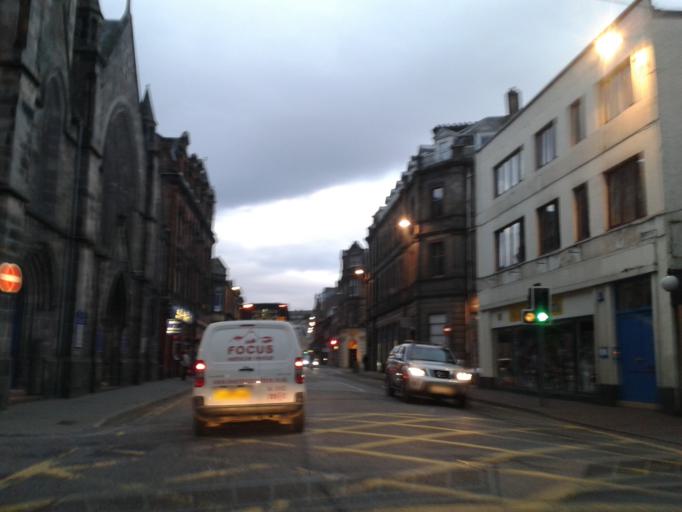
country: GB
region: Scotland
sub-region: Highland
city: Inverness
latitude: 57.4800
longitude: -4.2263
